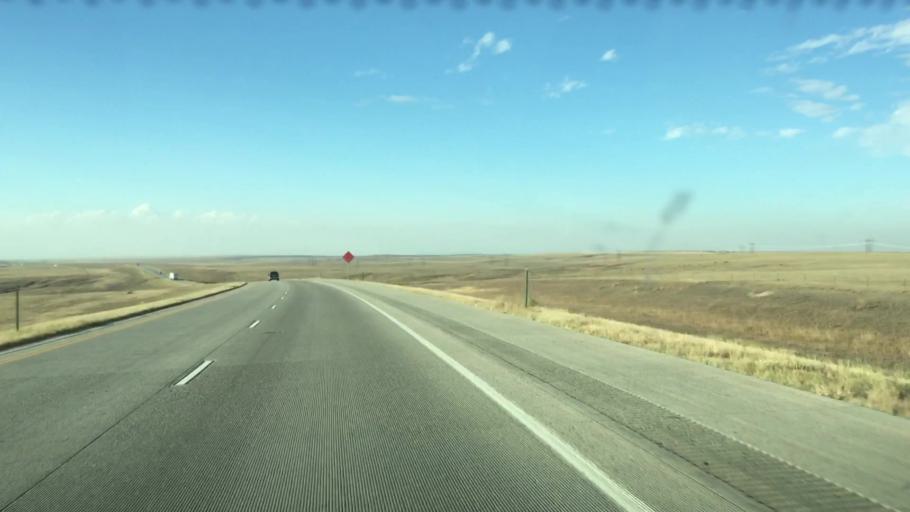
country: US
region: Colorado
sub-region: Lincoln County
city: Limon
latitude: 39.3940
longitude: -103.8899
